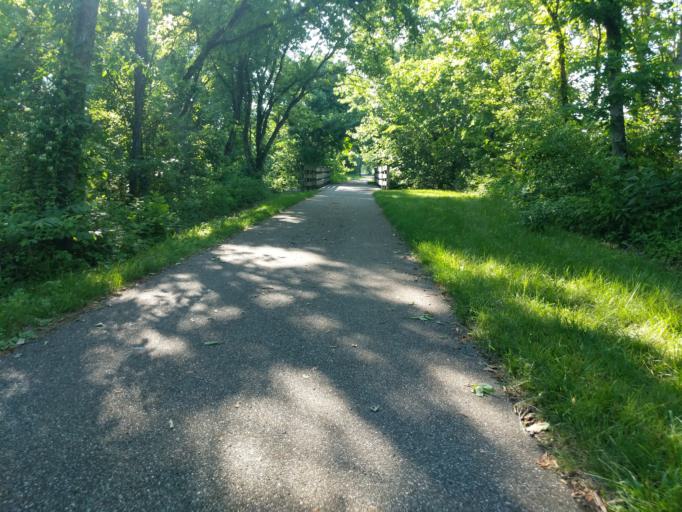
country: US
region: Ohio
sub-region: Athens County
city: Nelsonville
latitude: 39.4300
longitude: -82.2063
